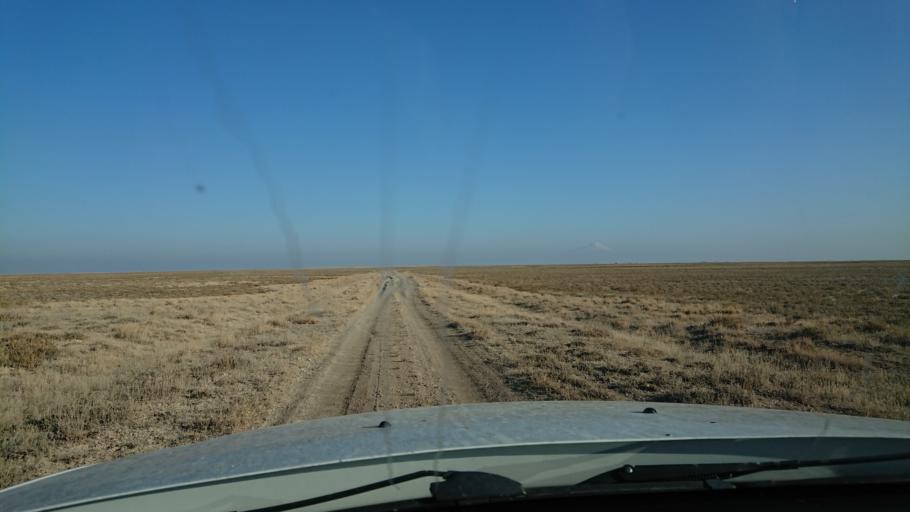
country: TR
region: Aksaray
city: Eskil
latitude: 38.4077
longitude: 33.5660
